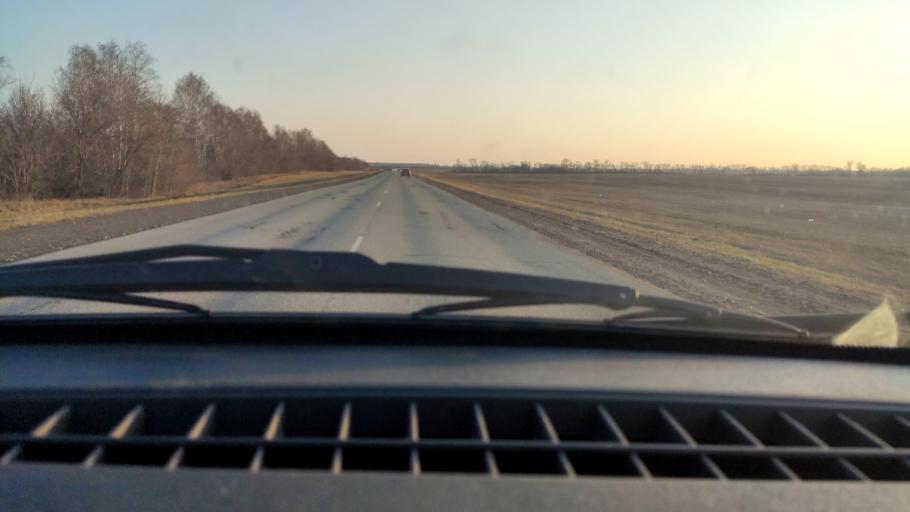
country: RU
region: Bashkortostan
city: Davlekanovo
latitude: 54.2856
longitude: 55.1145
